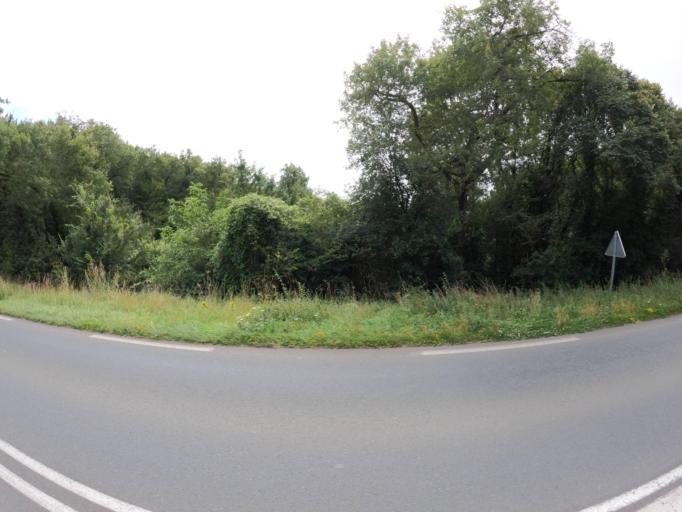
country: FR
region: Poitou-Charentes
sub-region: Departement de la Vienne
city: Chaunay
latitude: 46.1421
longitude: 0.2115
